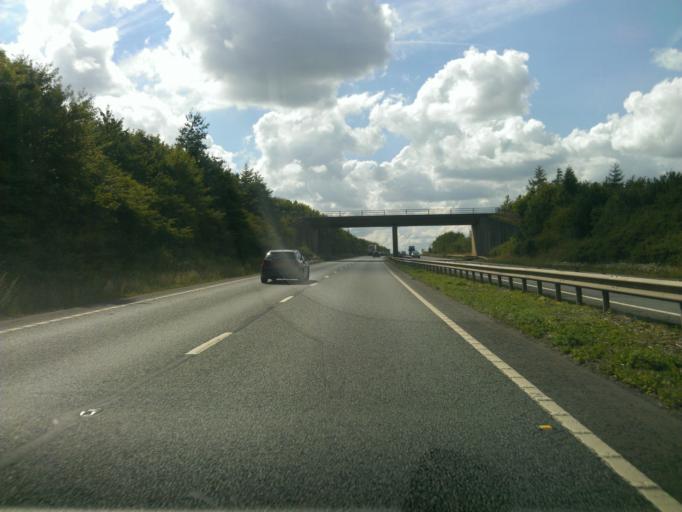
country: GB
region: England
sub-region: Northamptonshire
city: Desborough
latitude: 52.4046
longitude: -0.8584
